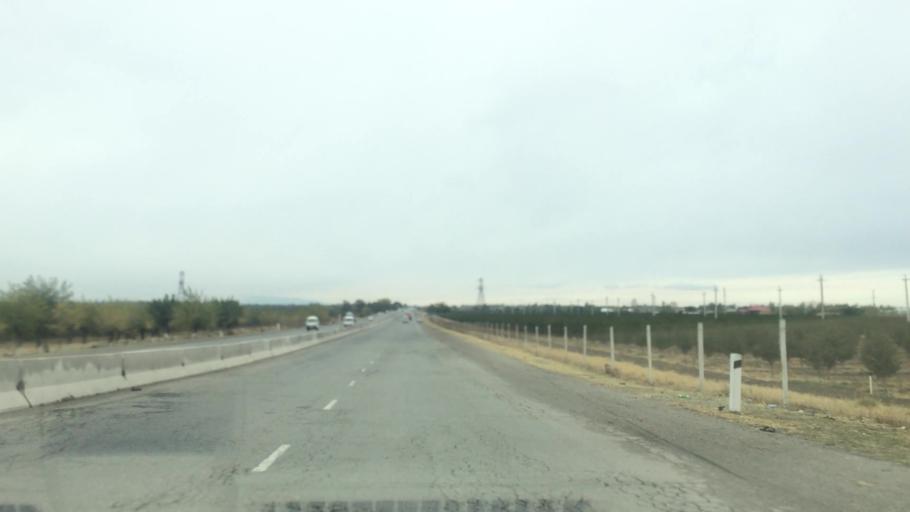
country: UZ
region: Samarqand
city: Bulung'ur
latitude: 39.7571
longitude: 67.2423
